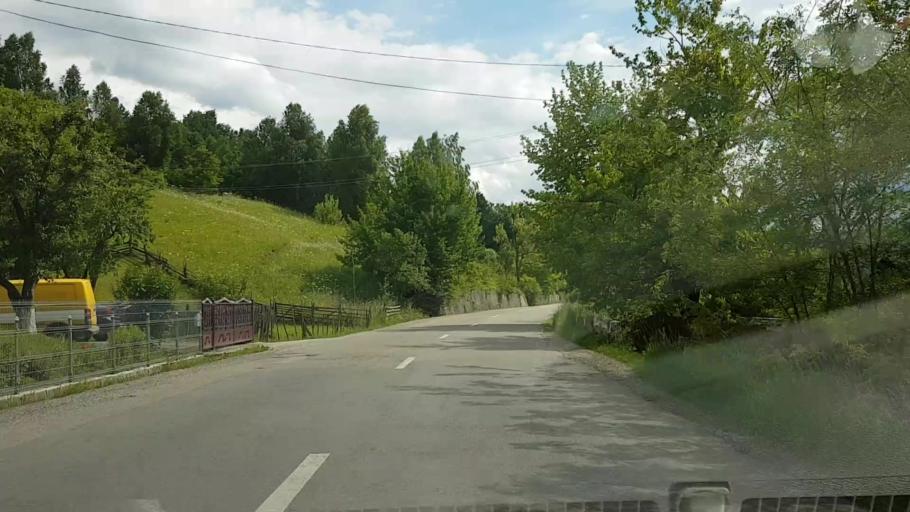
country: RO
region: Neamt
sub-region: Comuna Hangu
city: Hangu
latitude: 47.0323
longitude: 26.0666
